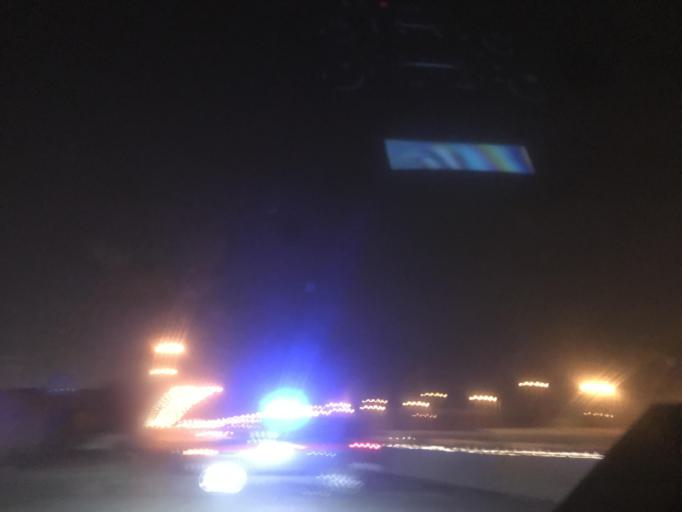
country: SA
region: Ar Riyad
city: Riyadh
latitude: 24.7572
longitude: 46.5901
